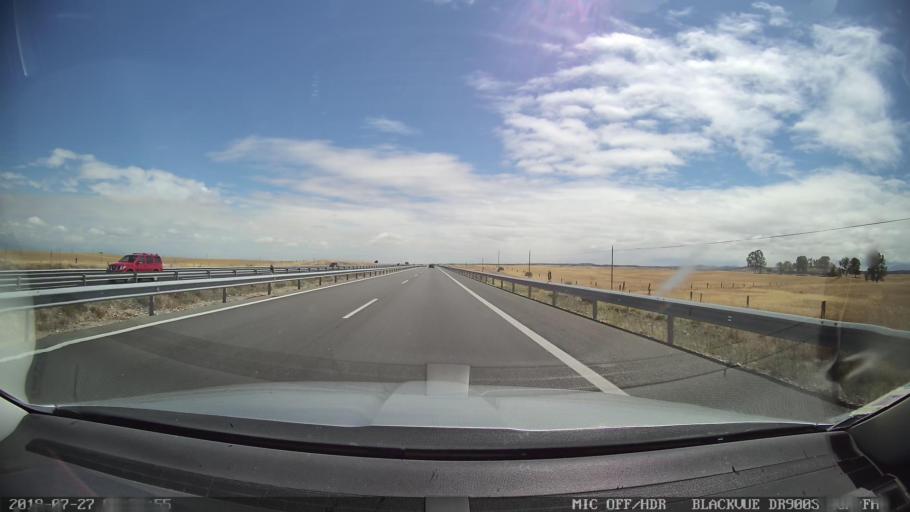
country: ES
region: Extremadura
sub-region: Provincia de Caceres
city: Berrocalejo
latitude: 39.8925
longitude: -5.3767
